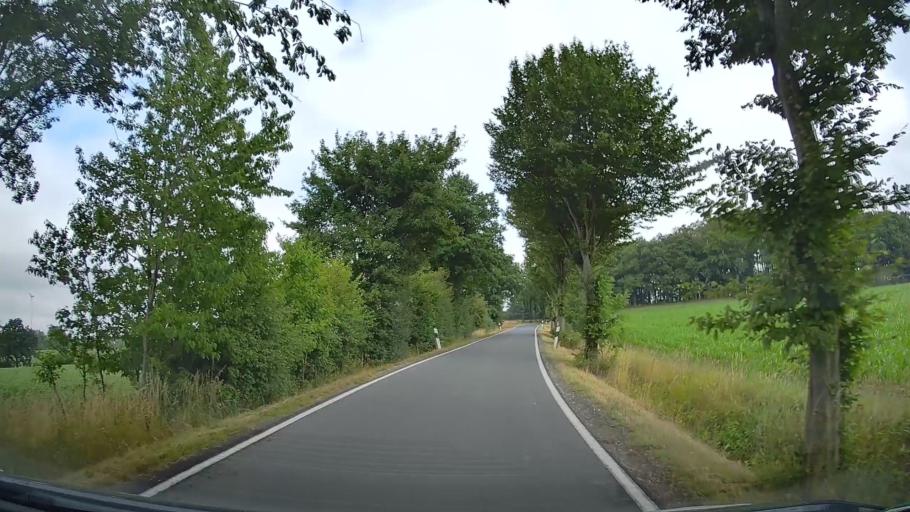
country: DE
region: North Rhine-Westphalia
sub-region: Regierungsbezirk Detmold
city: Barntrup
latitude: 52.0747
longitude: 9.1331
